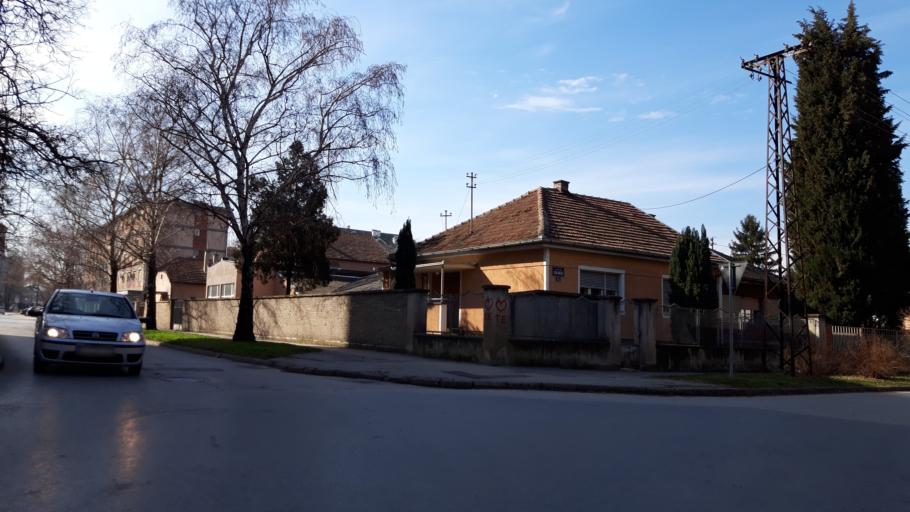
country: RS
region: Autonomna Pokrajina Vojvodina
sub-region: Juznobacki Okrug
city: Novi Sad
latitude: 45.2611
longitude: 19.8238
